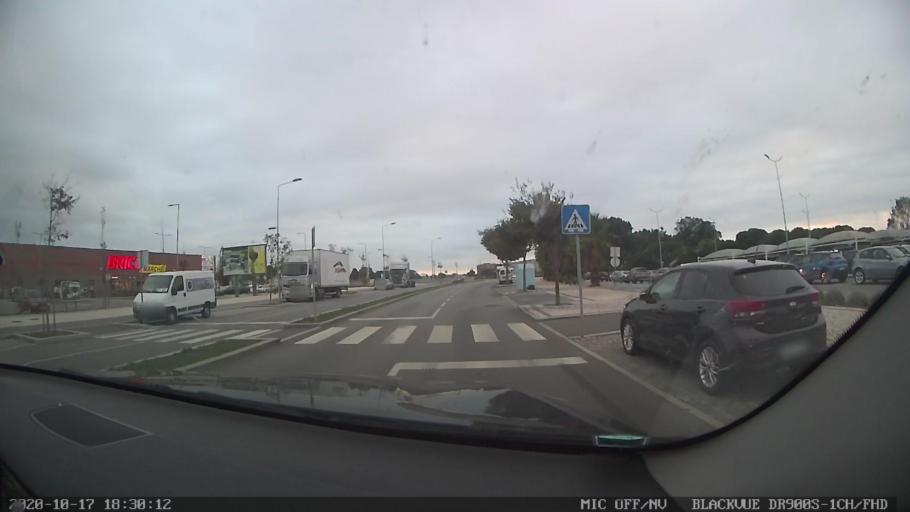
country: PT
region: Porto
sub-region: Vila do Conde
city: Vila do Conde
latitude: 41.3697
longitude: -8.7438
